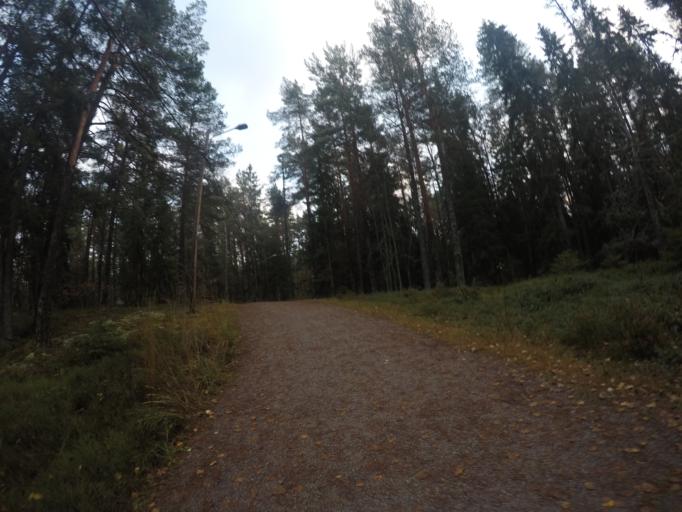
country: SE
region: Soedermanland
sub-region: Eskilstuna Kommun
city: Eskilstuna
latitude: 59.3469
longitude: 16.5255
